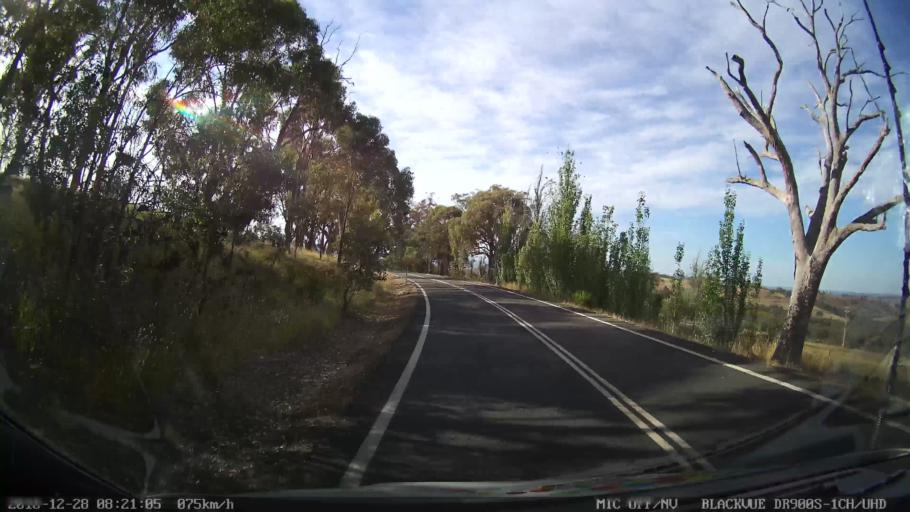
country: AU
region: New South Wales
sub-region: Blayney
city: Blayney
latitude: -33.8785
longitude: 149.3502
